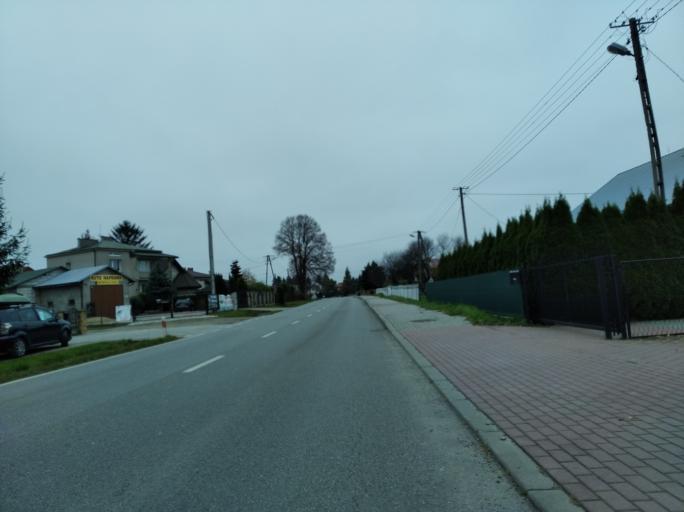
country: PL
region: Subcarpathian Voivodeship
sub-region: Powiat krosnienski
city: Chorkowka
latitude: 49.6791
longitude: 21.7153
